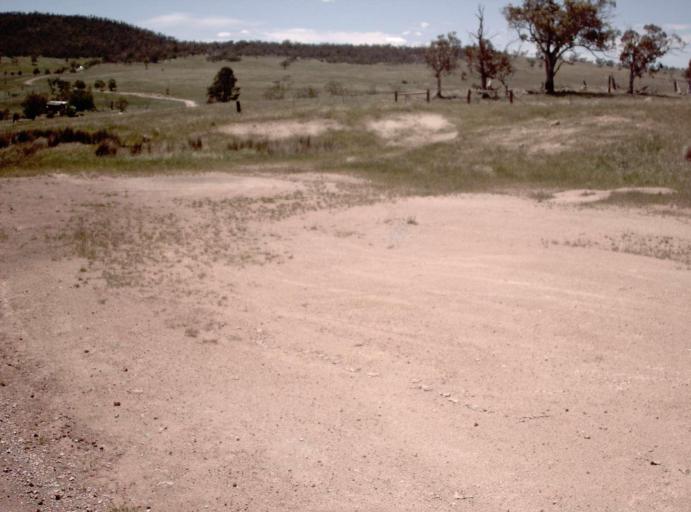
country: AU
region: New South Wales
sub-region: Snowy River
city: Jindabyne
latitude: -37.0151
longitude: 148.2755
